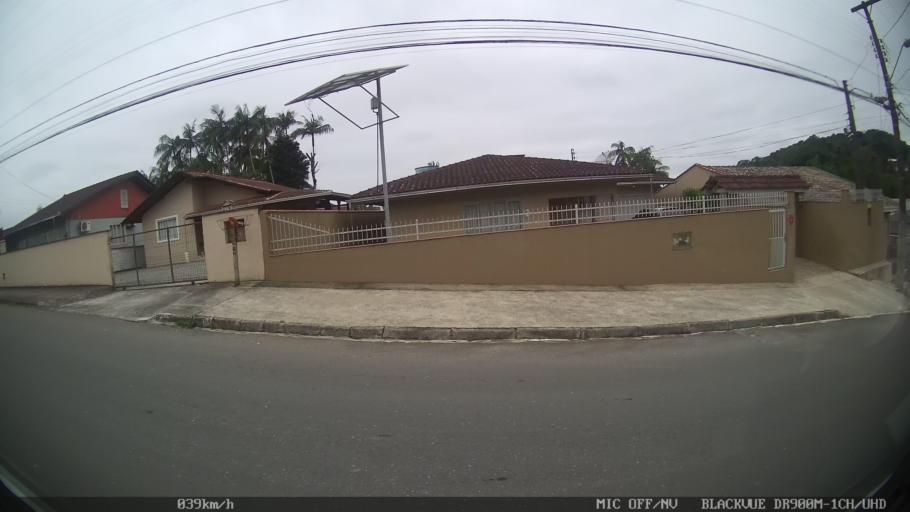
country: BR
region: Santa Catarina
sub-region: Joinville
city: Joinville
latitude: -26.2702
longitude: -48.8866
